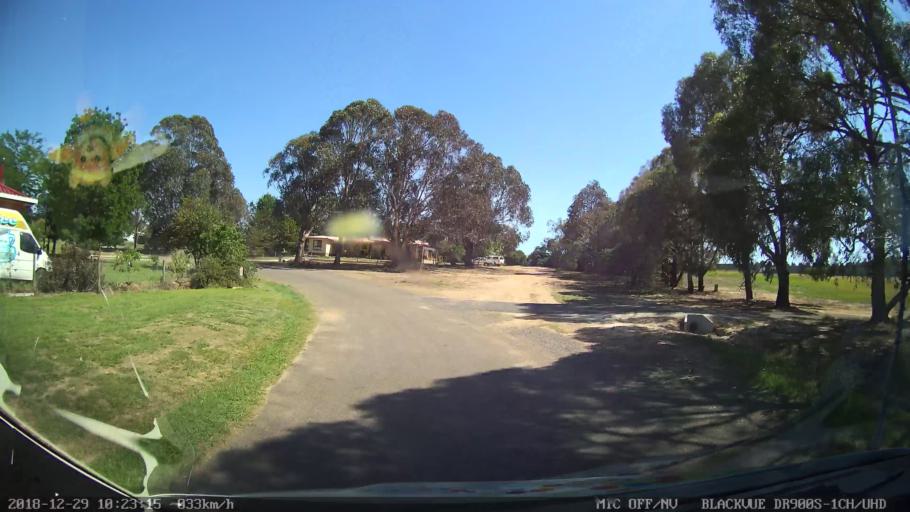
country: AU
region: New South Wales
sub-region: Yass Valley
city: Gundaroo
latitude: -34.9146
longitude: 149.4385
